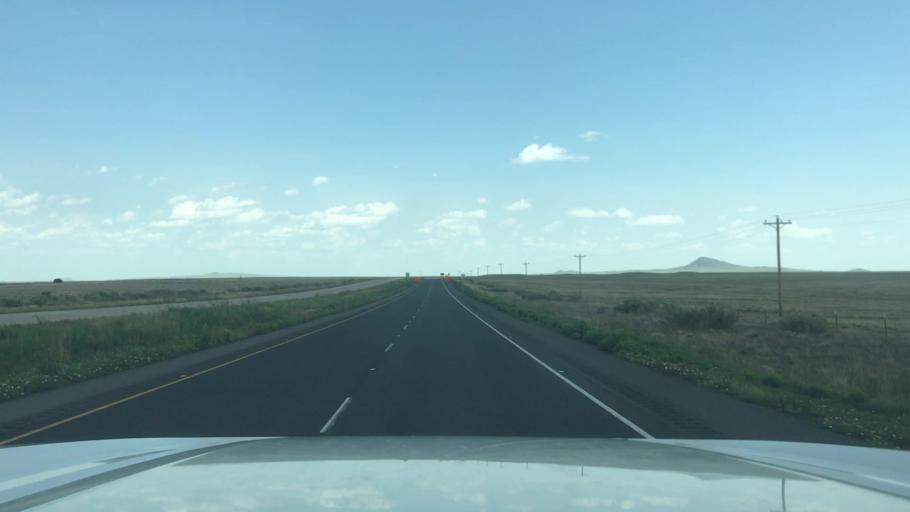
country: US
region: New Mexico
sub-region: Union County
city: Clayton
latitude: 36.6198
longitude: -103.6943
